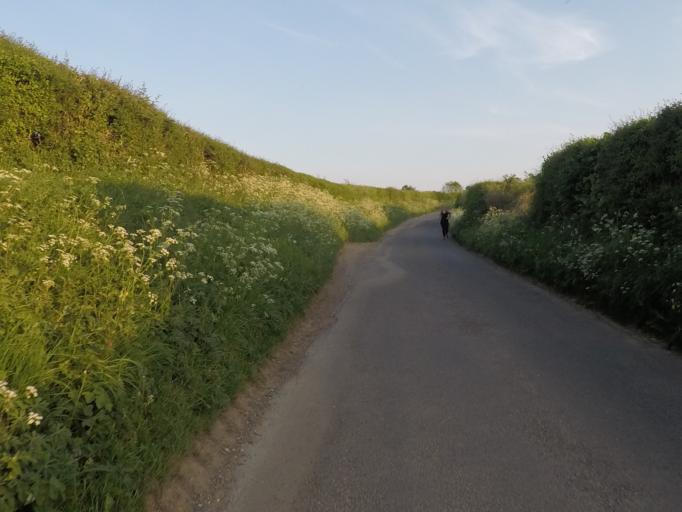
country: GB
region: England
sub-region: Oxfordshire
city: Charlbury
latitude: 51.8403
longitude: -1.5325
